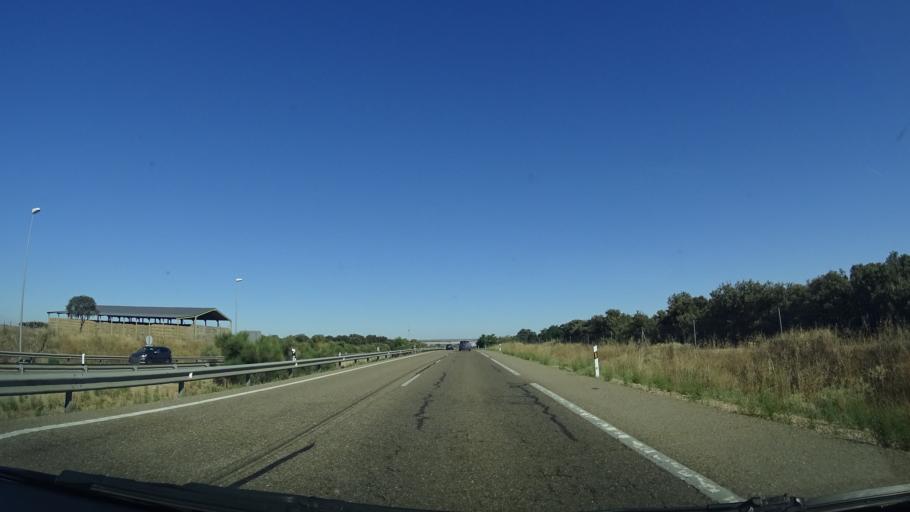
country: ES
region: Castille and Leon
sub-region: Provincia de Valladolid
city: San Pedro de Latarce
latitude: 41.7776
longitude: -5.3150
